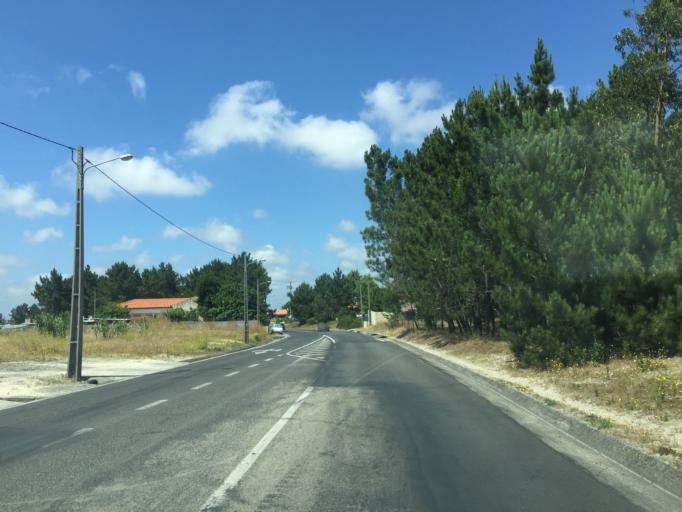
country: PT
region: Leiria
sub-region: Marinha Grande
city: Marinha Grande
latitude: 39.7310
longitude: -8.9301
